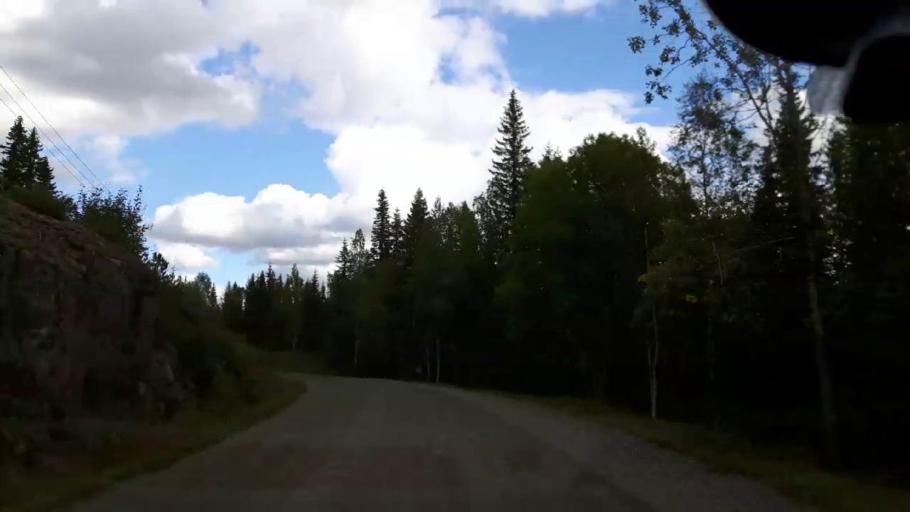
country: SE
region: Jaemtland
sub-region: Stroemsunds Kommun
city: Stroemsund
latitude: 63.4166
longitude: 15.8566
